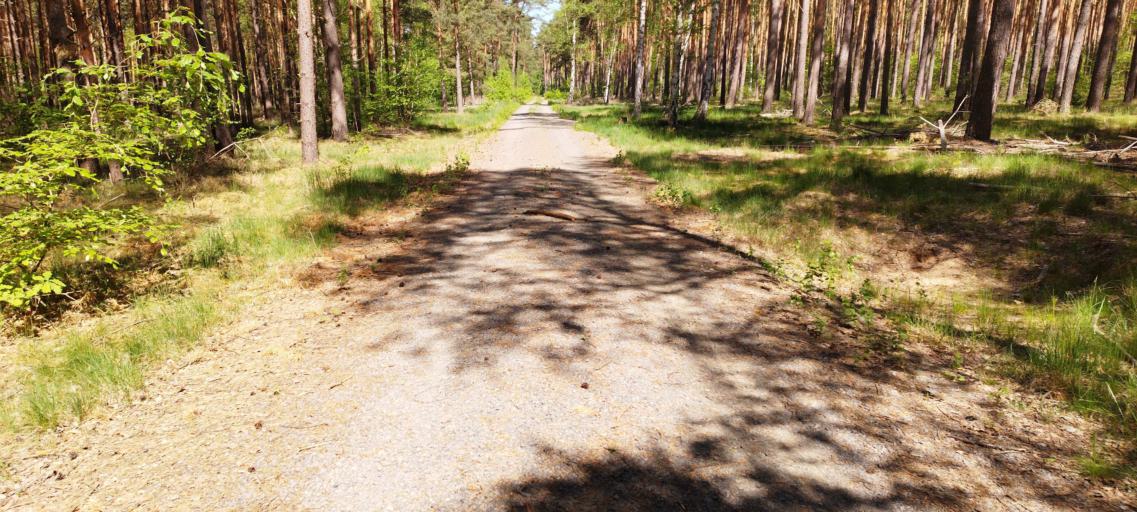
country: DE
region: Berlin
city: Muggelheim
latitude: 52.4021
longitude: 13.6959
